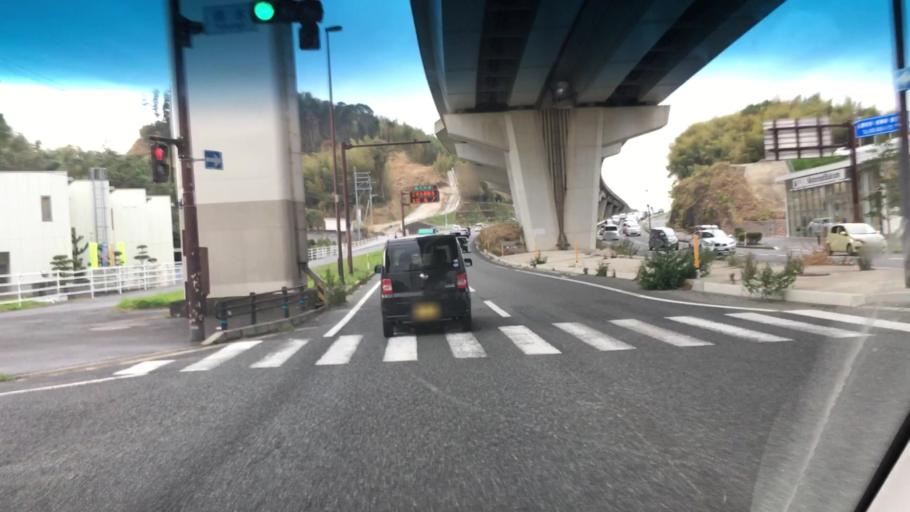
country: JP
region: Fukuoka
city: Maebaru-chuo
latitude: 33.5732
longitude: 130.2572
